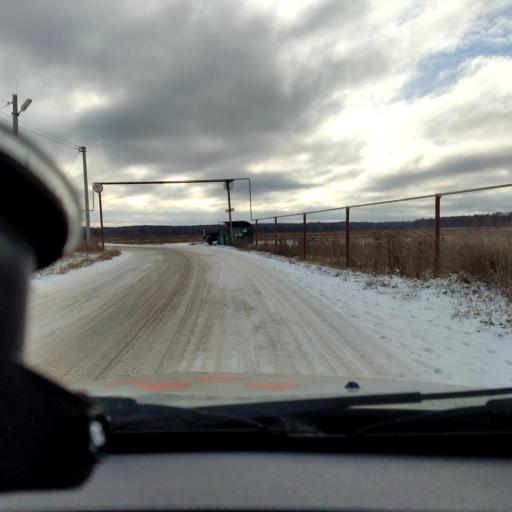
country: RU
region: Bashkortostan
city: Avdon
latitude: 54.7844
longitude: 55.7278
